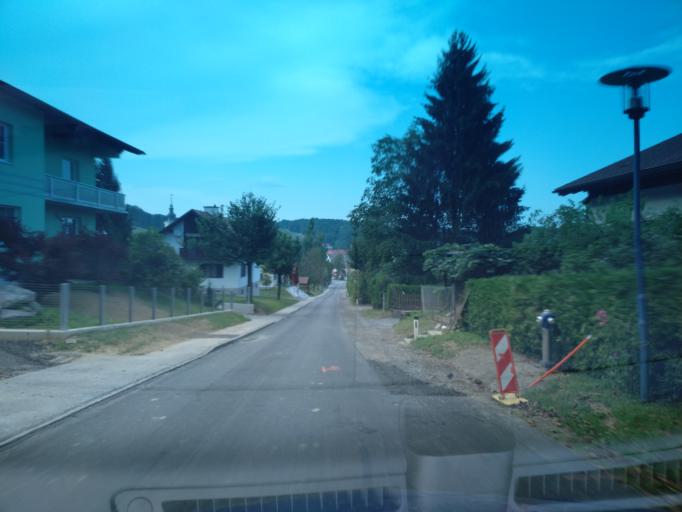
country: AT
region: Styria
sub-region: Politischer Bezirk Deutschlandsberg
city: Wies
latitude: 46.7155
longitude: 15.2734
